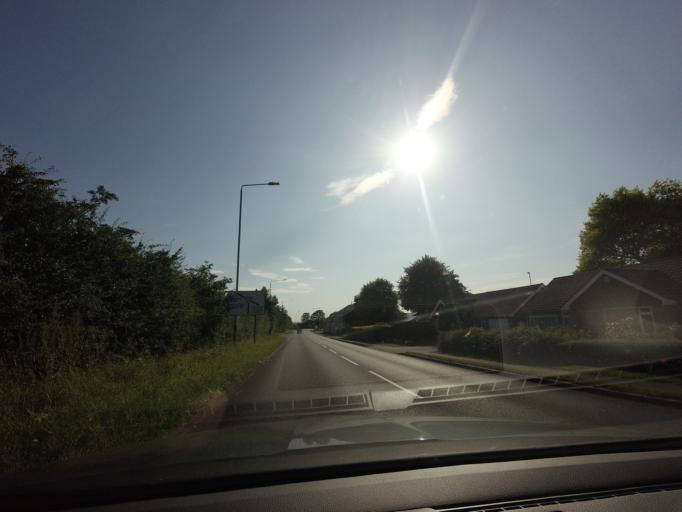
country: GB
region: England
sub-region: Derbyshire
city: Pinxton
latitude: 53.0515
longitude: -1.2923
